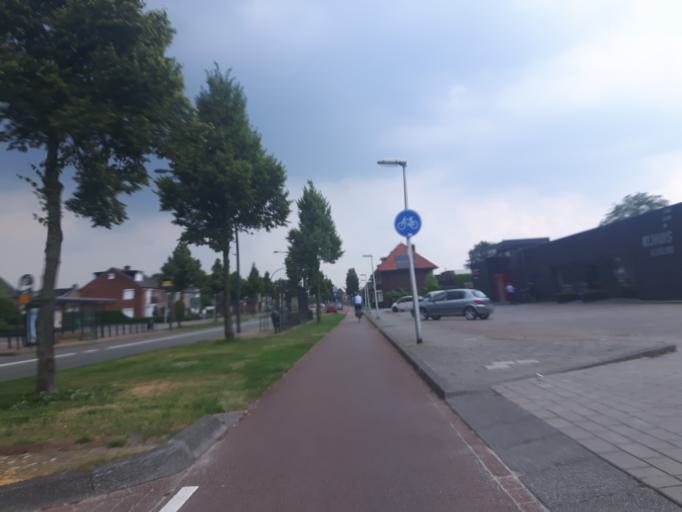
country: NL
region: Overijssel
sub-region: Gemeente Hengelo
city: Hengelo
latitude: 52.2721
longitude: 6.8117
